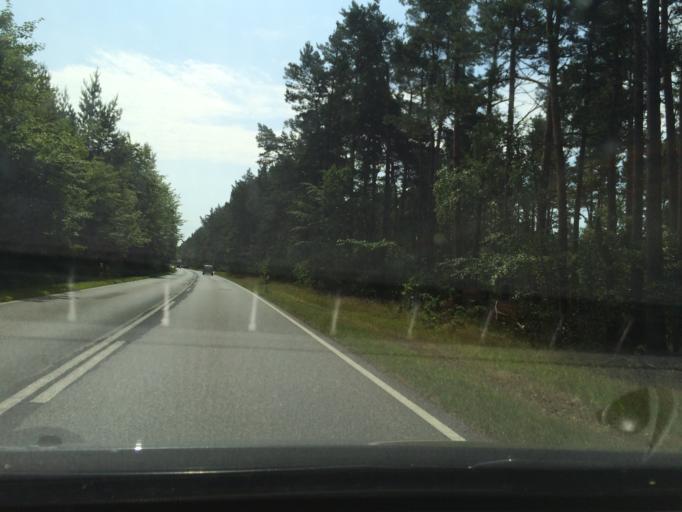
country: DE
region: Mecklenburg-Vorpommern
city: Ostseebad Binz
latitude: 54.4287
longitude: 13.5753
